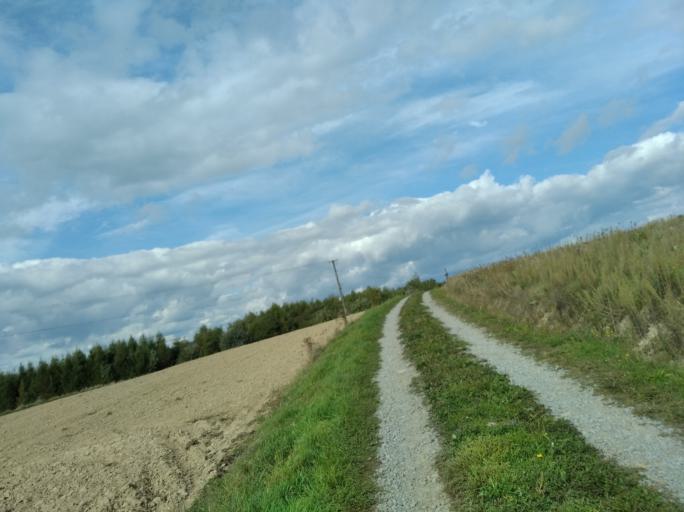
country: PL
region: Subcarpathian Voivodeship
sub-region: Powiat strzyzowski
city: Jawornik
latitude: 49.8340
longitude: 21.9012
